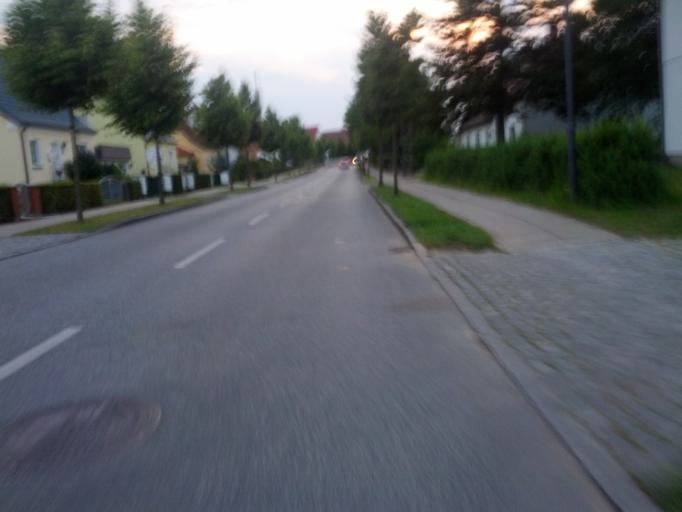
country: DE
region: Mecklenburg-Vorpommern
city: Ostseebad Kuhlungsborn
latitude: 54.1433
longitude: 11.7412
